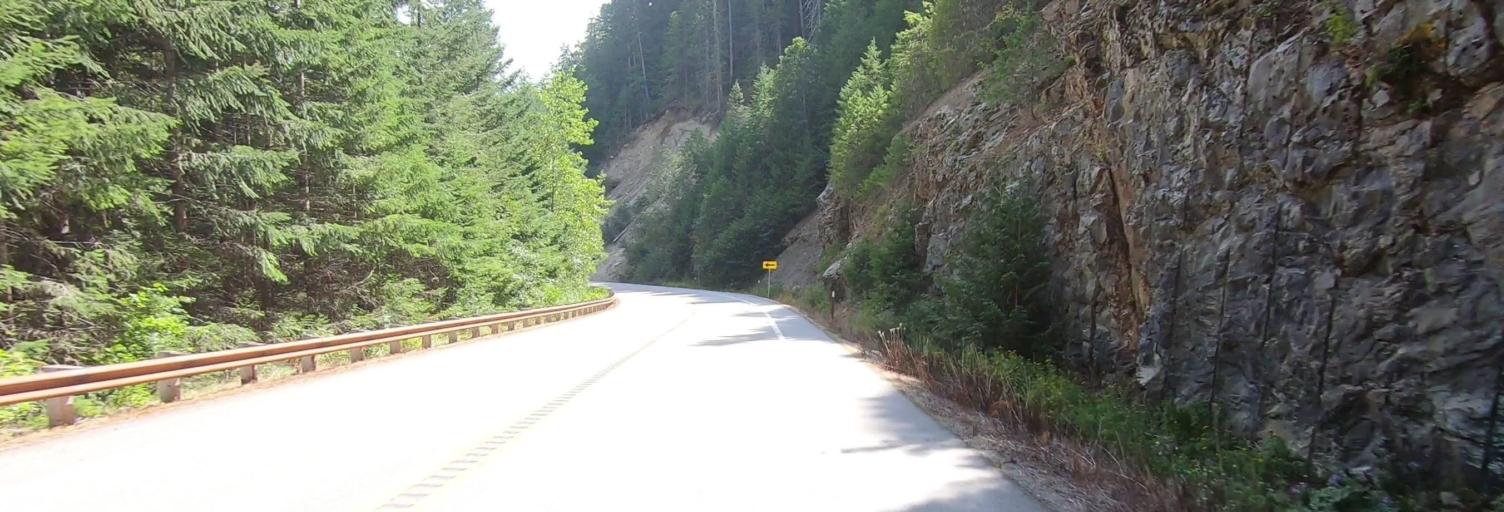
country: US
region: Washington
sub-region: Snohomish County
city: Darrington
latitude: 48.6867
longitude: -120.9093
